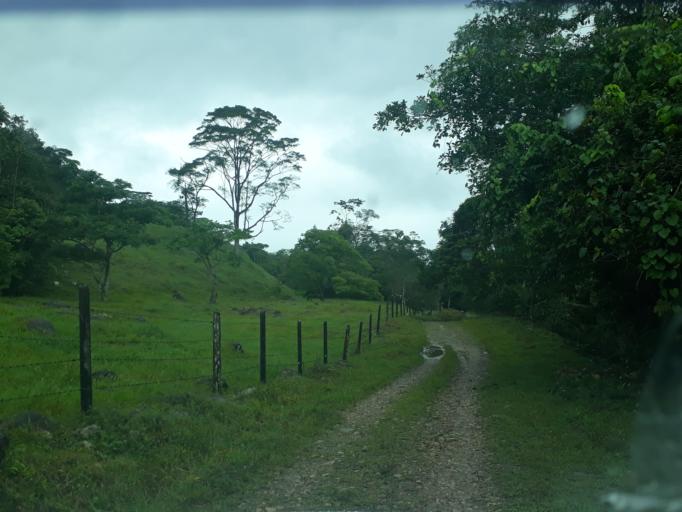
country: CO
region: Cundinamarca
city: Medina
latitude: 4.5274
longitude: -73.3649
